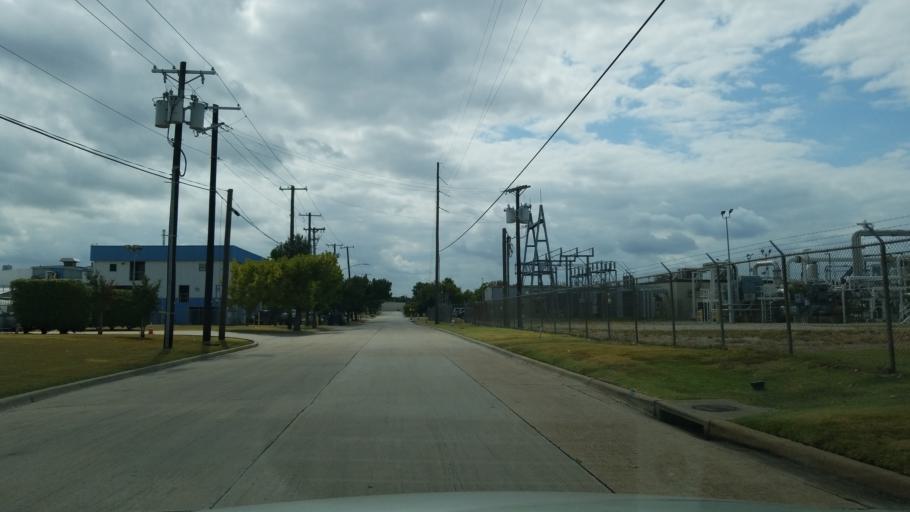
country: US
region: Texas
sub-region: Dallas County
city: Garland
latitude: 32.8902
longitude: -96.6735
